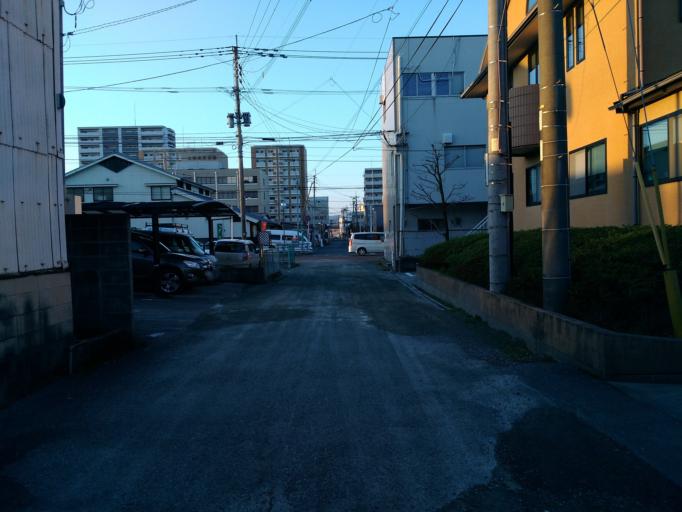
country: JP
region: Saga Prefecture
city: Saga-shi
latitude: 33.2605
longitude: 130.3034
